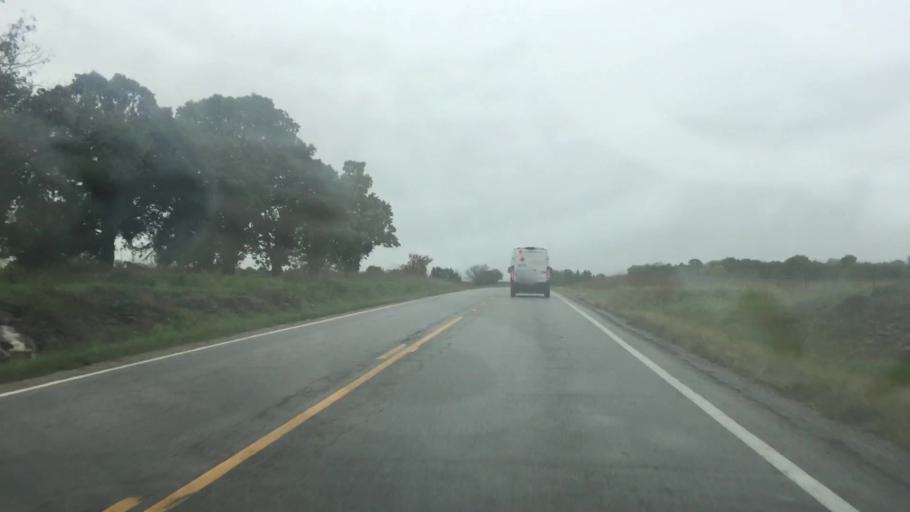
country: US
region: Kansas
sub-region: Anderson County
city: Garnett
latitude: 38.2462
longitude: -95.2483
